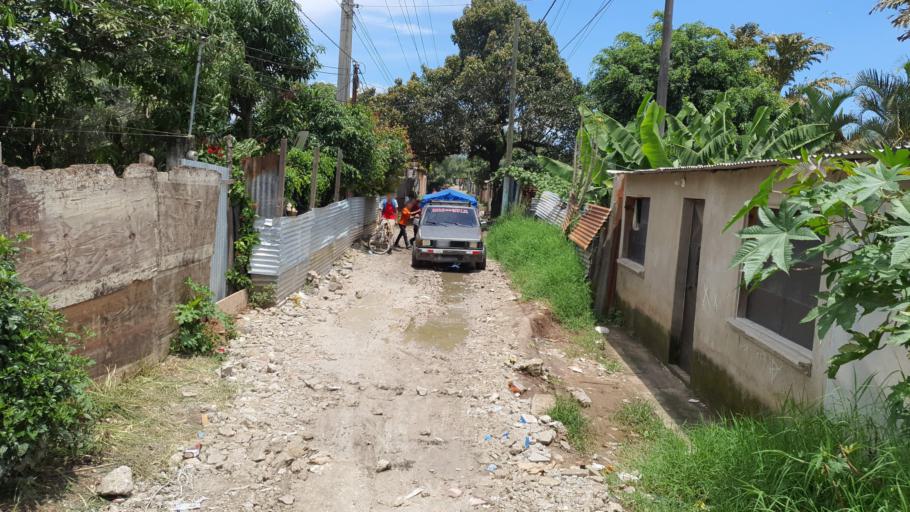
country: GT
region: Guatemala
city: Villa Canales
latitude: 14.4934
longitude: -90.5399
